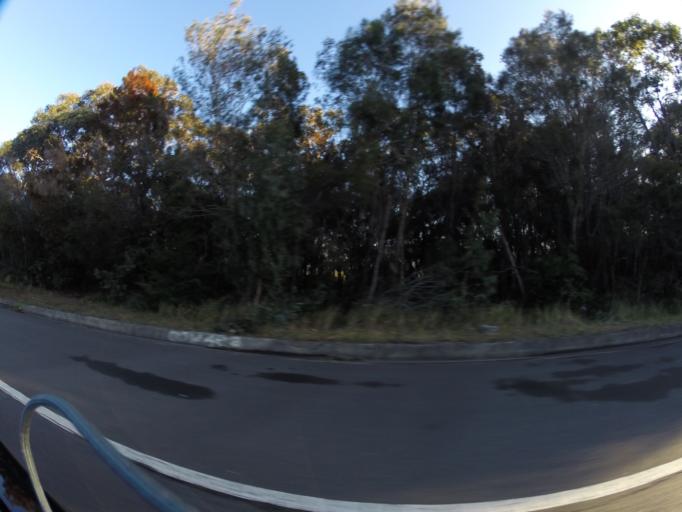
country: AU
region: New South Wales
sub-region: Sutherland Shire
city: Loftus
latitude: -34.0566
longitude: 151.0404
